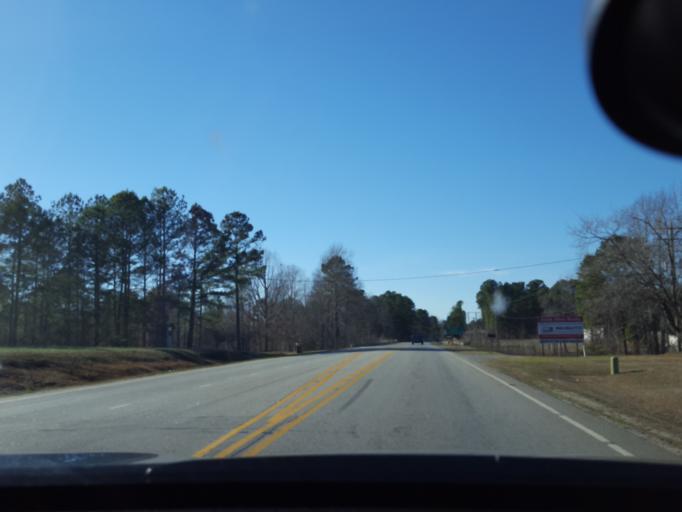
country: US
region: North Carolina
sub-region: Halifax County
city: South Rosemary
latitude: 36.4580
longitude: -77.8099
